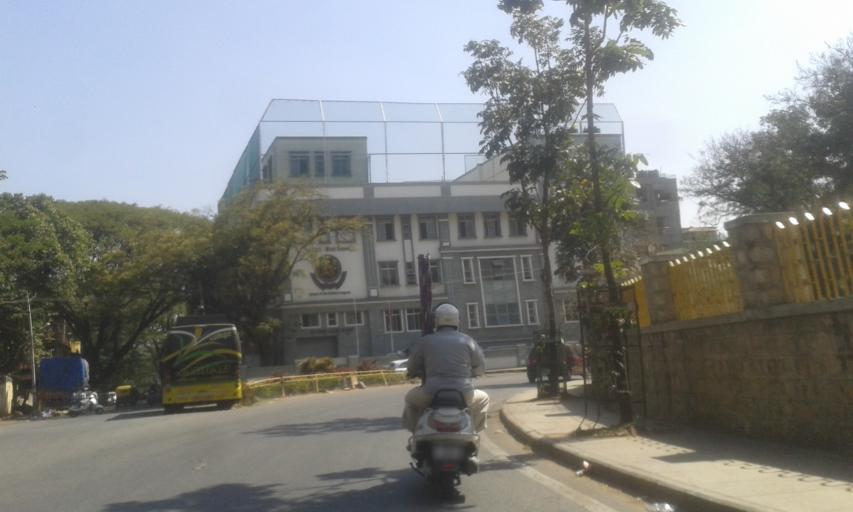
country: IN
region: Karnataka
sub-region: Bangalore Urban
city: Bangalore
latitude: 12.9405
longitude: 77.5773
